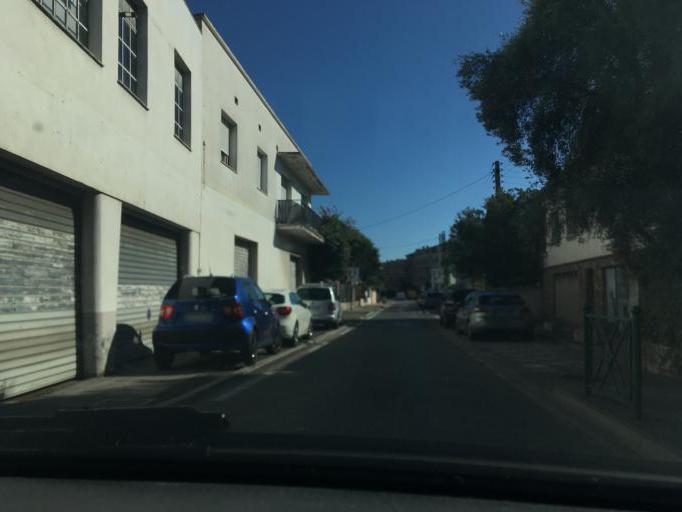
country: FR
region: Provence-Alpes-Cote d'Azur
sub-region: Departement du Var
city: Sainte-Maxime
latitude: 43.3135
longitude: 6.6352
